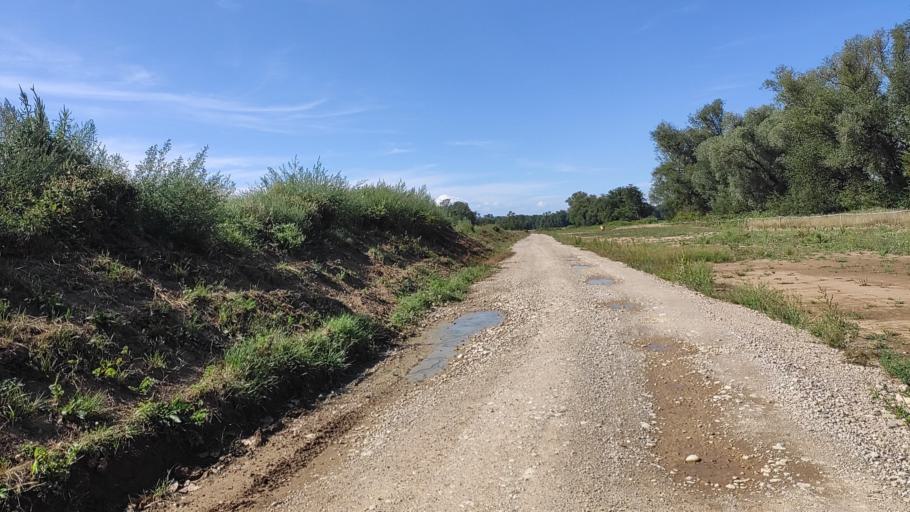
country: DE
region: Baden-Wuerttemberg
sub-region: Freiburg Region
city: Umkirch
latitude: 48.0088
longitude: 7.7948
